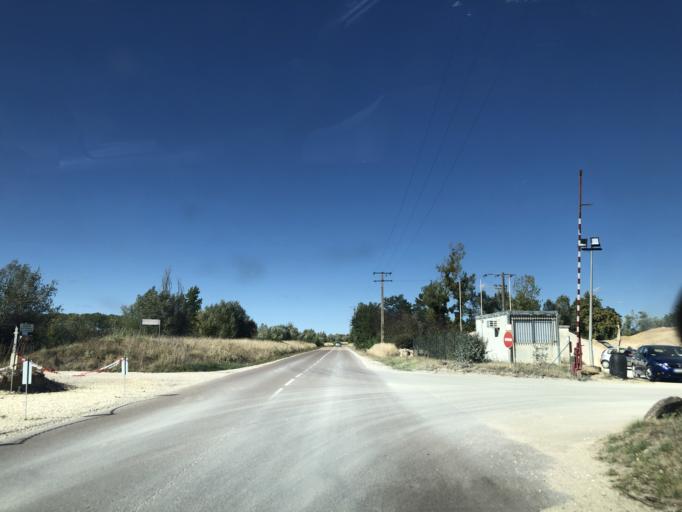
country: FR
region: Bourgogne
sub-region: Departement de l'Yonne
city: Appoigny
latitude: 47.8882
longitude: 3.5444
